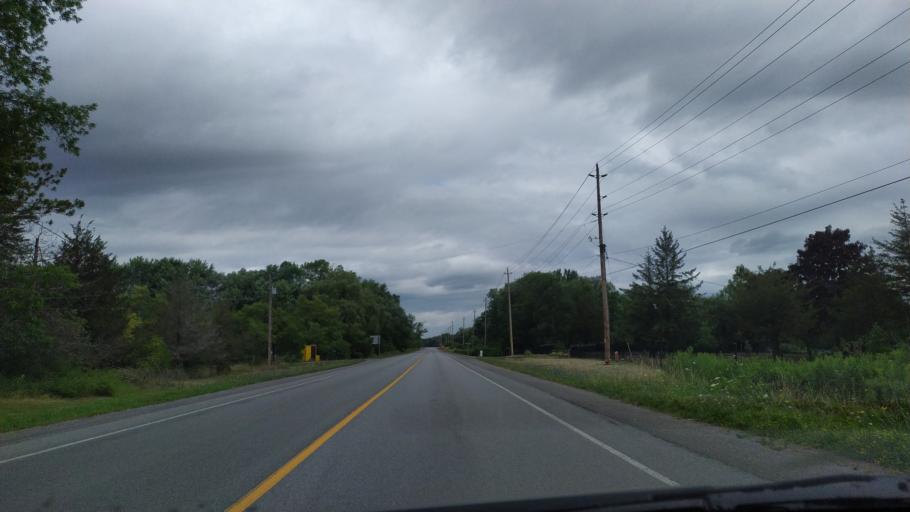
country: CA
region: Ontario
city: Quinte West
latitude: 43.9927
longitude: -77.5175
